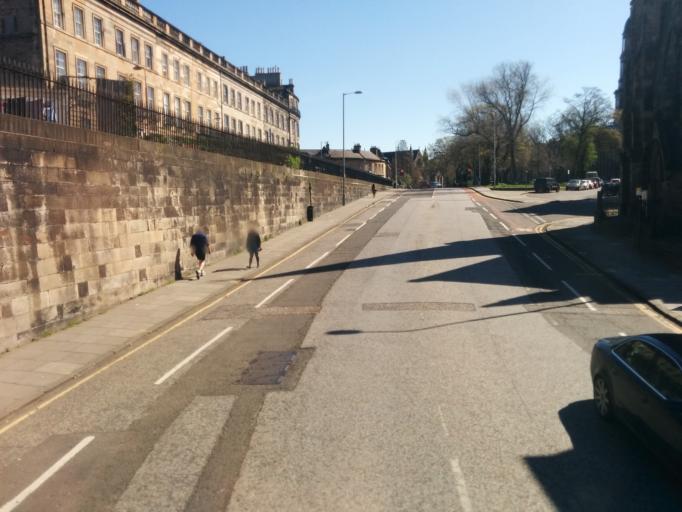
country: GB
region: Scotland
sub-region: Edinburgh
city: Edinburgh
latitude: 55.9617
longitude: -3.1949
